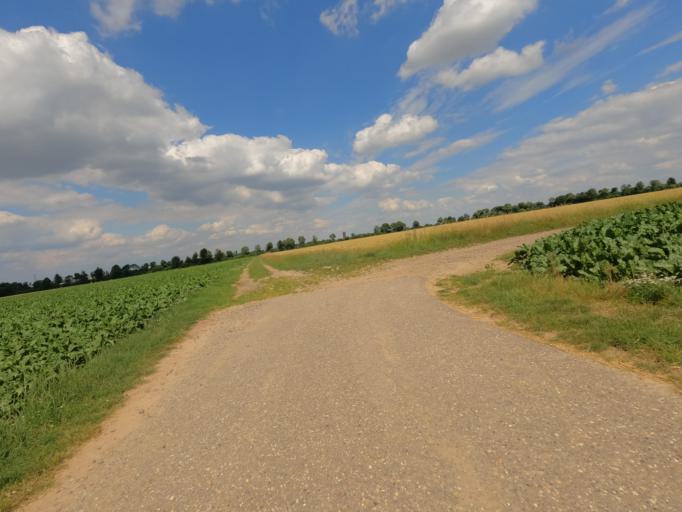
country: DE
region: North Rhine-Westphalia
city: Geilenkirchen
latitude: 50.9620
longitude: 6.0871
